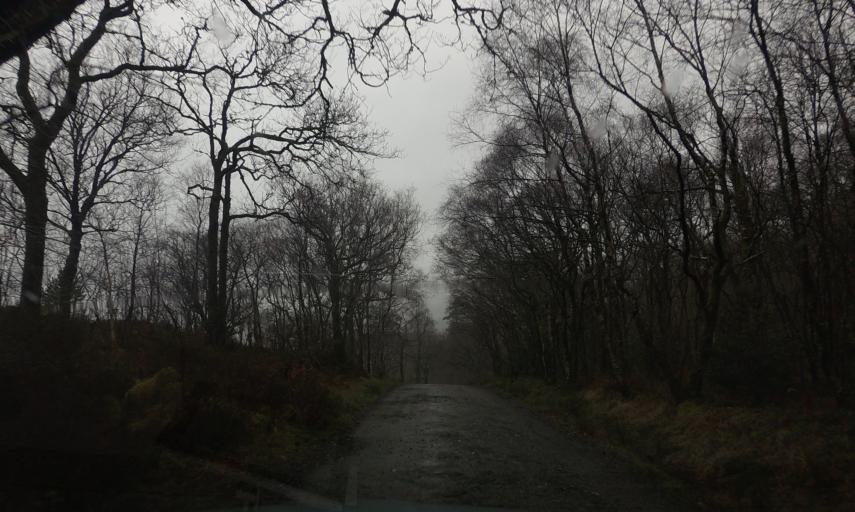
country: GB
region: Scotland
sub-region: West Dunbartonshire
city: Balloch
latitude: 56.1550
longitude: -4.6425
